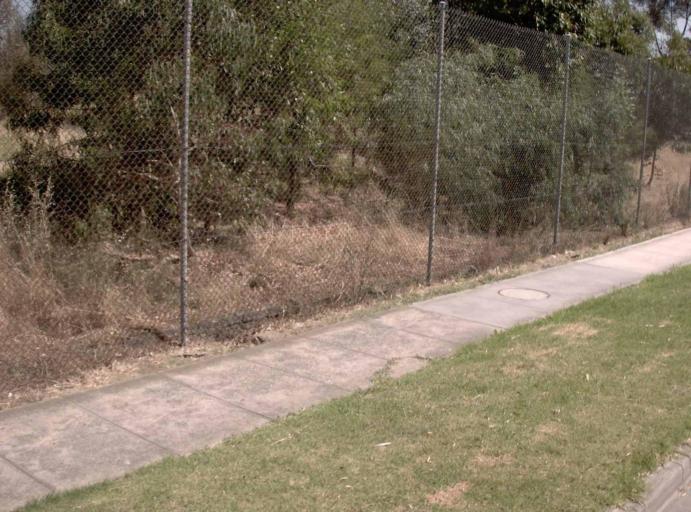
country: AU
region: Victoria
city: Ashburton
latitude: -37.8732
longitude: 145.0919
